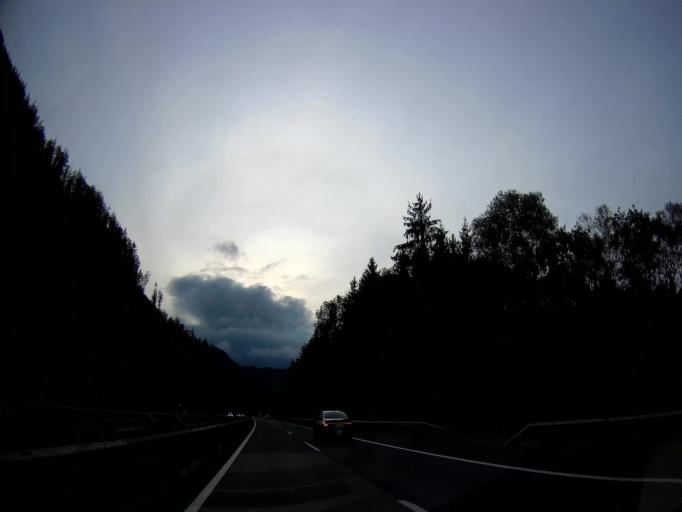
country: AT
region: Styria
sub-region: Politischer Bezirk Graz-Umgebung
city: Frohnleiten
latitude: 47.2202
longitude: 15.2920
